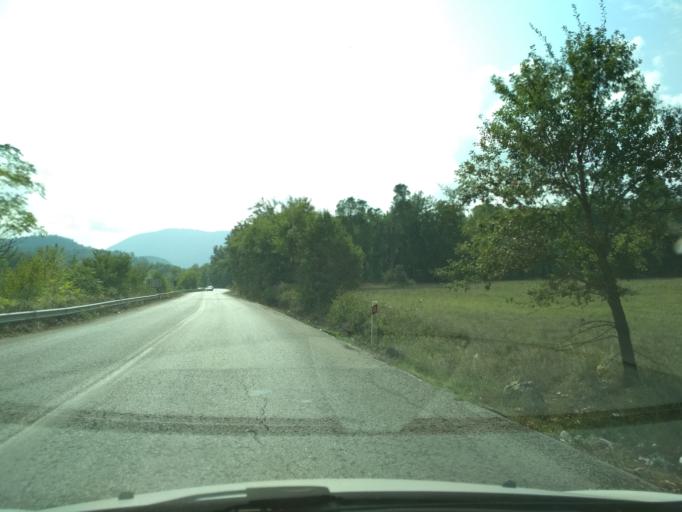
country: GR
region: Central Greece
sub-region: Nomos Evvoias
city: Prokopion
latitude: 38.7311
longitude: 23.4989
